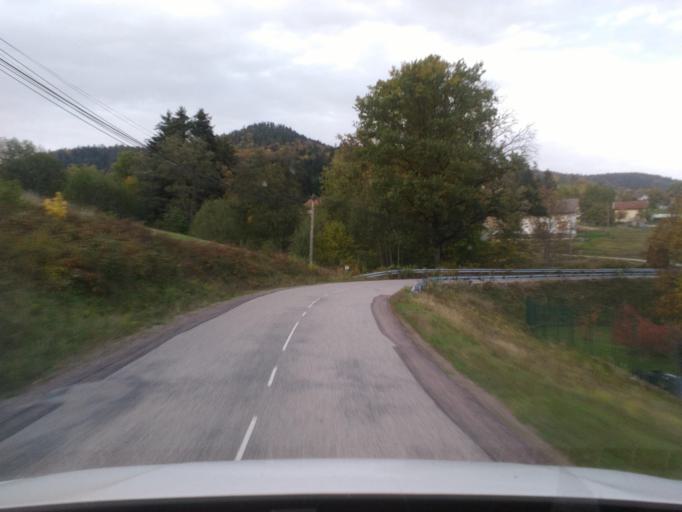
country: FR
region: Lorraine
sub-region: Departement des Vosges
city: Saint-Ame
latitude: 48.0411
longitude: 6.6719
